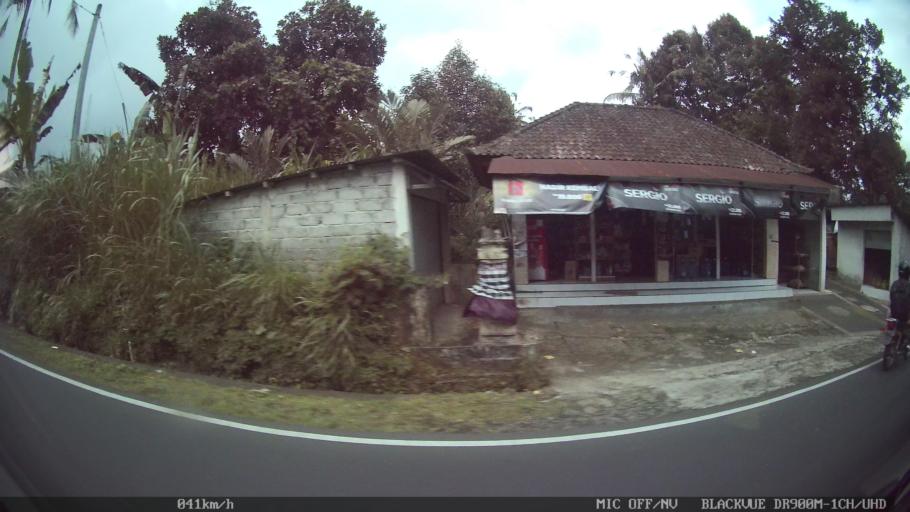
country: ID
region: Bali
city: Banjar Tiga
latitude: -8.3872
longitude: 115.4179
